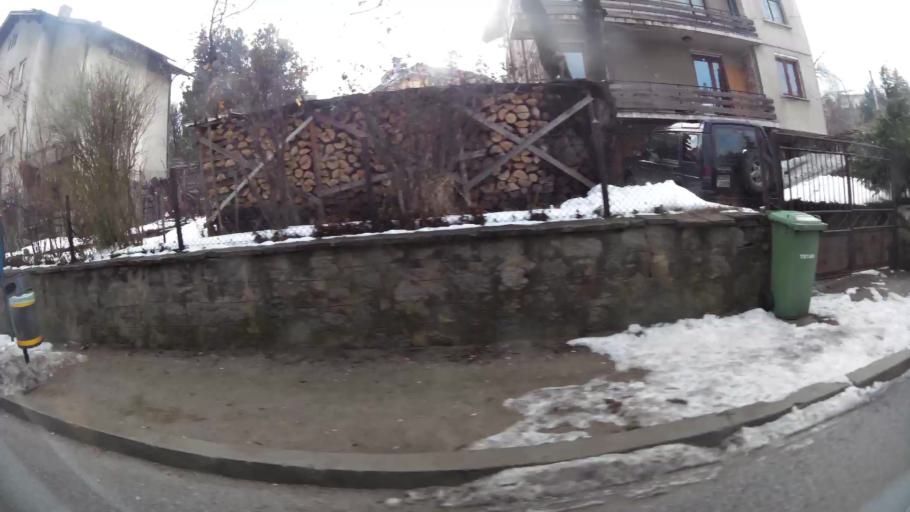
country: BG
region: Sofia-Capital
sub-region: Stolichna Obshtina
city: Sofia
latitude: 42.6455
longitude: 23.2726
